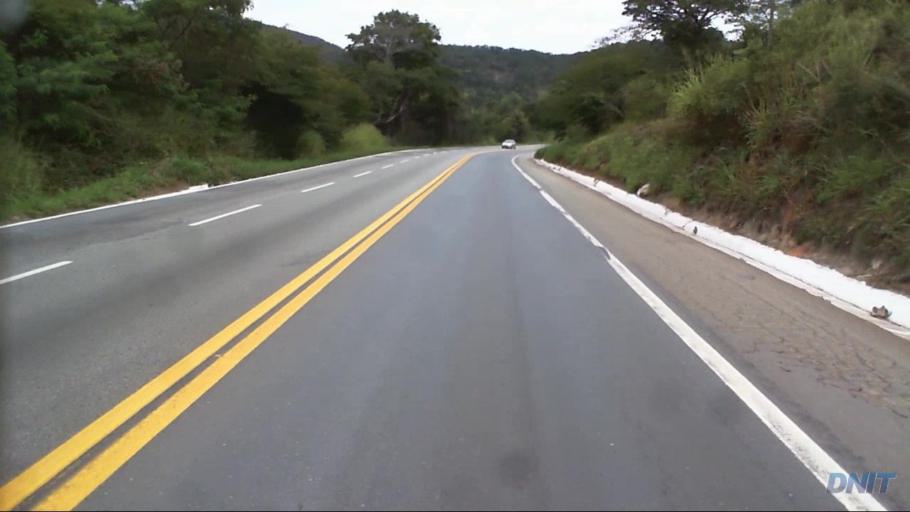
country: BR
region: Minas Gerais
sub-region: Caete
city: Caete
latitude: -19.7857
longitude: -43.7242
